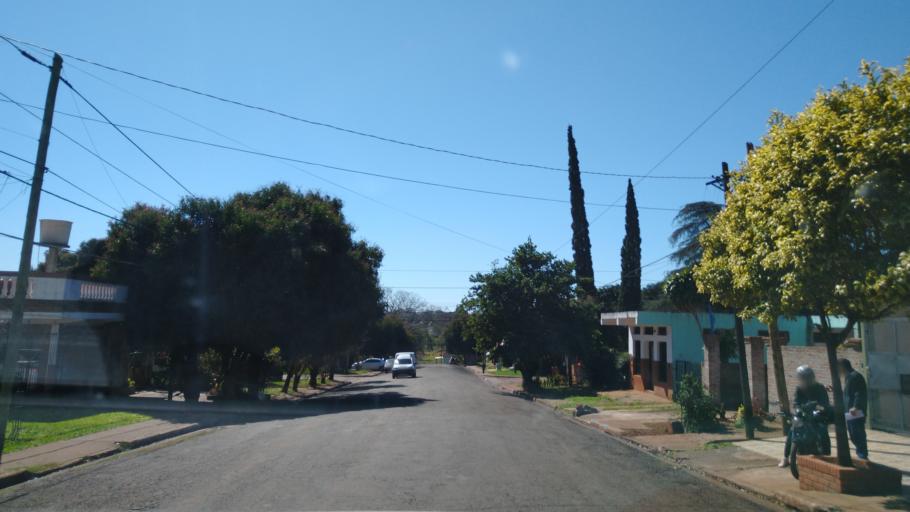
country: AR
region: Misiones
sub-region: Departamento de Capital
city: Posadas
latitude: -27.3964
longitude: -55.9338
